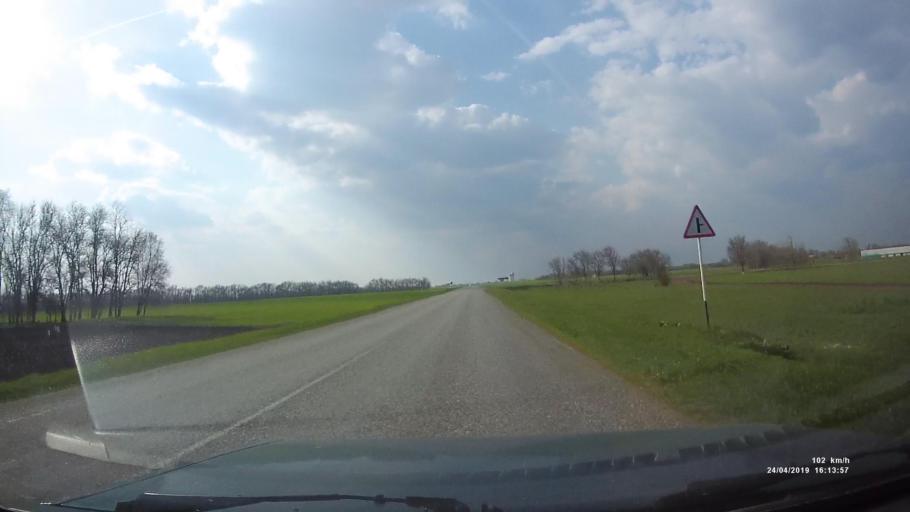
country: RU
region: Rostov
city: Sovetskoye
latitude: 46.7473
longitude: 42.2103
